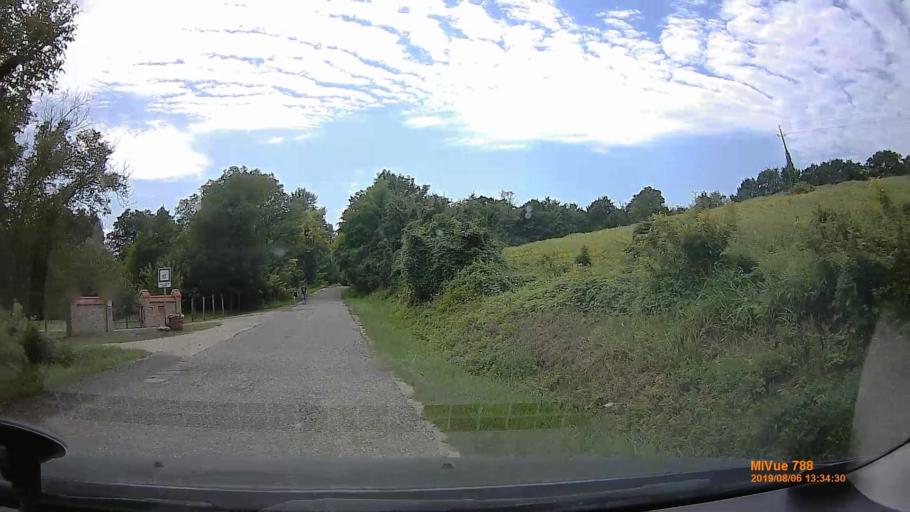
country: HU
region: Zala
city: Zalakomar
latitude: 46.5770
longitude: 17.1146
